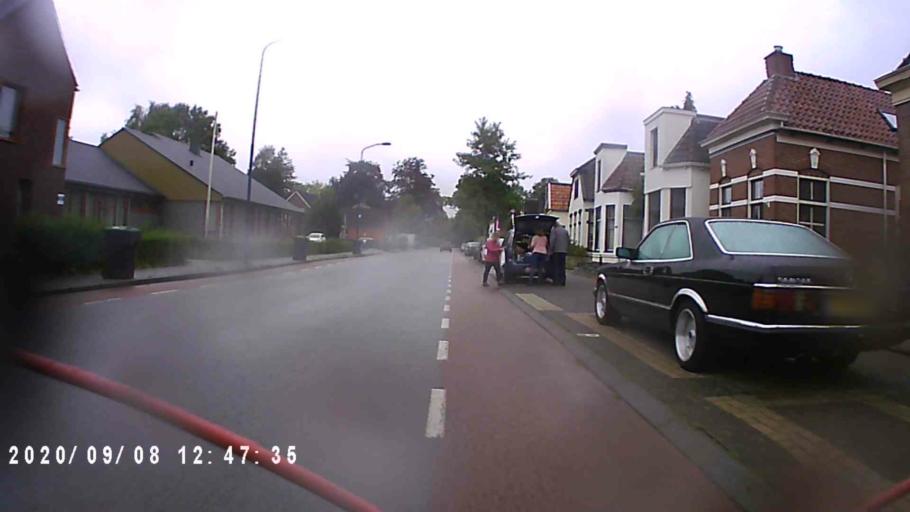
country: NL
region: Groningen
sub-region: Gemeente Veendam
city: Veendam
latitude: 53.1103
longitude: 6.8829
